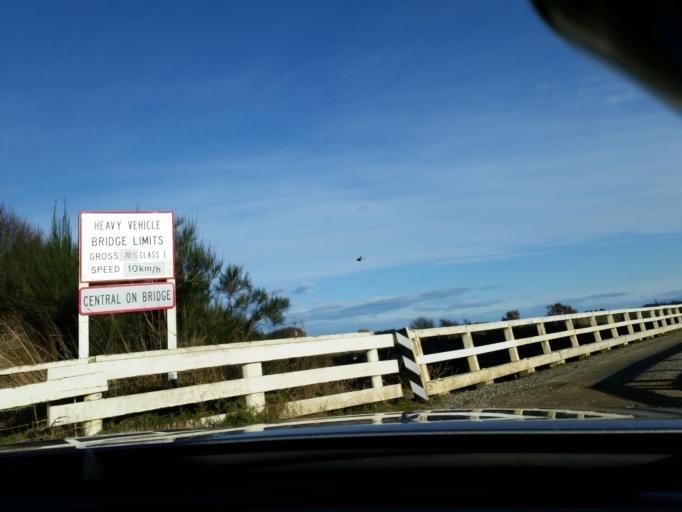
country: NZ
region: Southland
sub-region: Southland District
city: Winton
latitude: -46.2420
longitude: 168.4776
